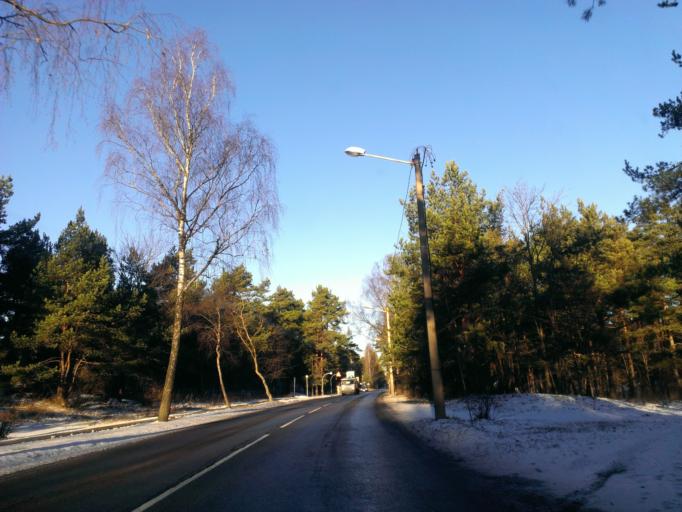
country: LV
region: Riga
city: Bolderaja
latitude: 57.0400
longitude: 24.1034
